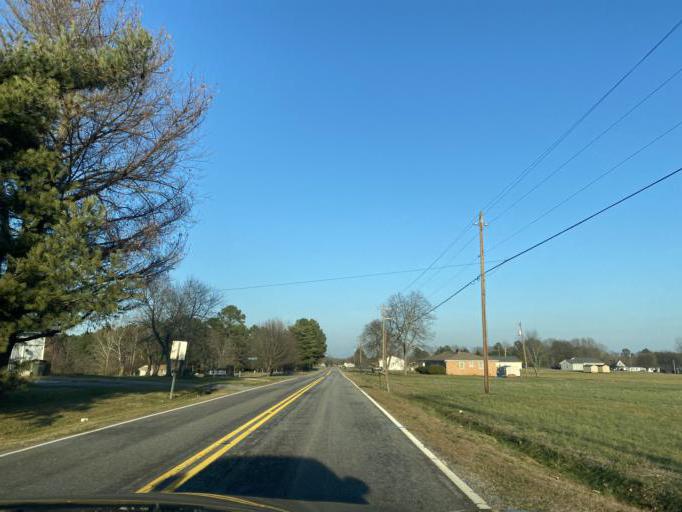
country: US
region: South Carolina
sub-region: Cherokee County
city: Gaffney
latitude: 35.1058
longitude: -81.6743
